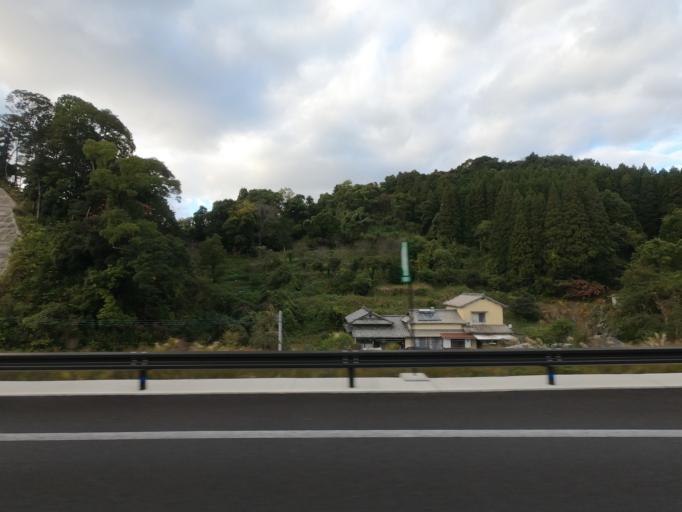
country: JP
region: Kumamoto
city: Minamata
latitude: 32.2271
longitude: 130.4376
